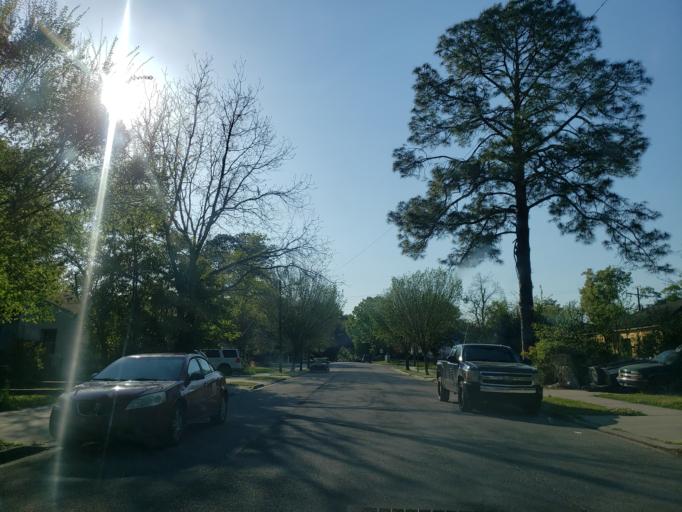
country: US
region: Georgia
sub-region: Chatham County
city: Thunderbolt
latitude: 32.0397
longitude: -81.0877
